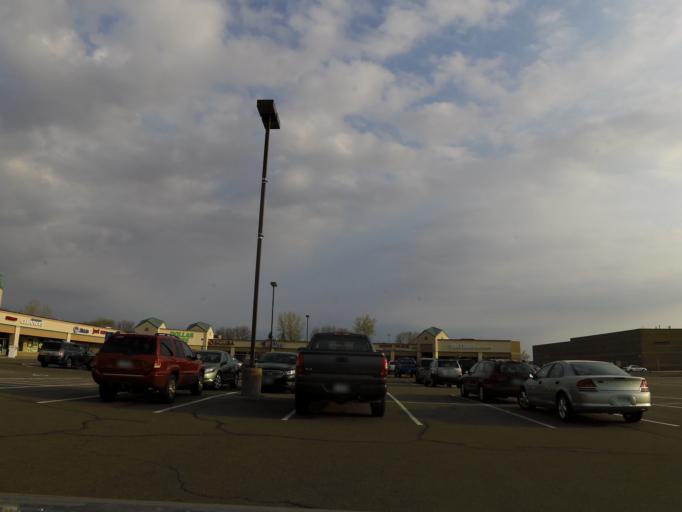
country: US
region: Minnesota
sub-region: Washington County
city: Oakdale
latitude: 44.9613
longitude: -92.9622
